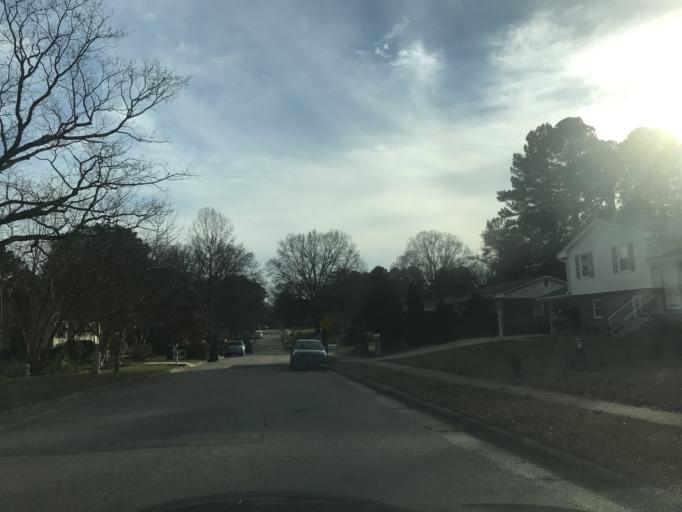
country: US
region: North Carolina
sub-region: Wake County
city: Raleigh
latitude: 35.8327
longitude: -78.5930
